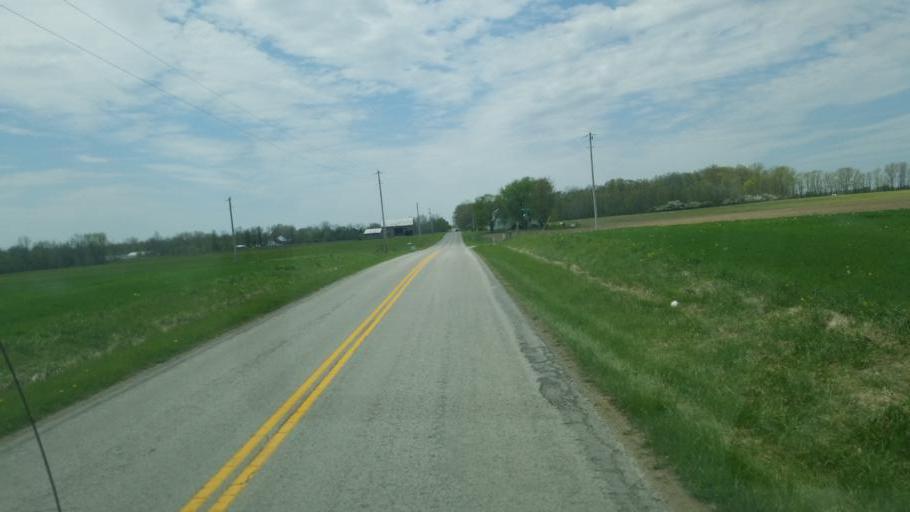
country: US
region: Ohio
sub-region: Hardin County
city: Ada
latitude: 40.7927
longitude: -83.9174
